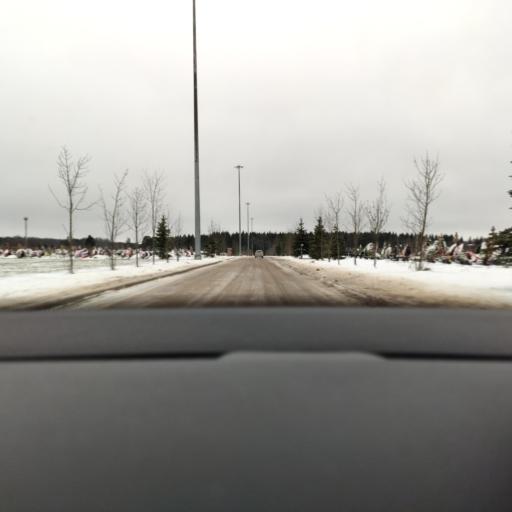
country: RU
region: Moskovskaya
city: Alabushevo
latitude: 56.0137
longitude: 37.1379
